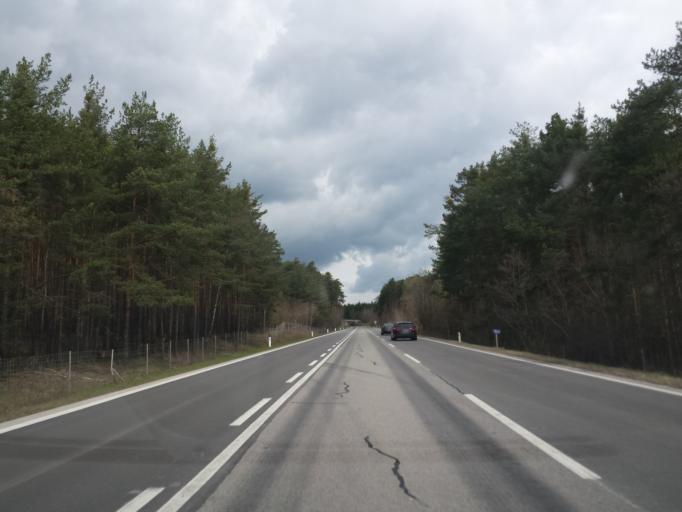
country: AT
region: Lower Austria
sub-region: Politischer Bezirk Krems
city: Lengenfeld
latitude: 48.4827
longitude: 15.5806
